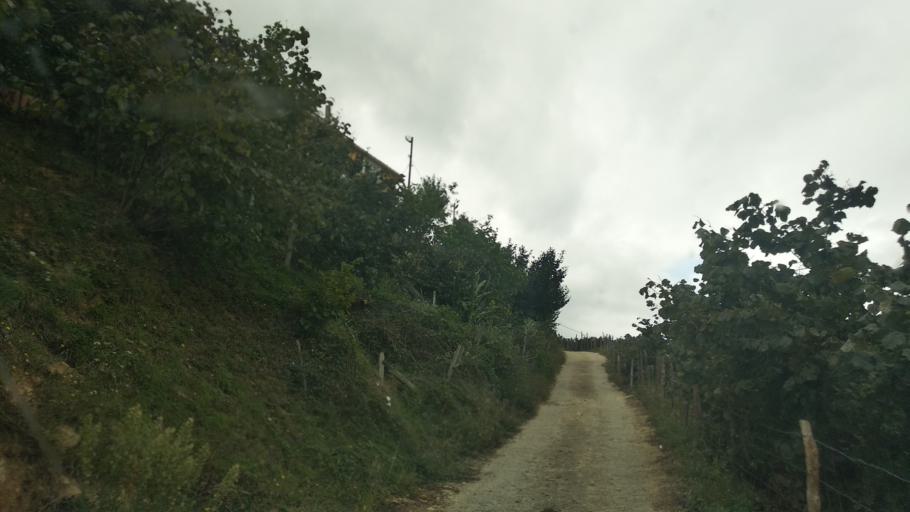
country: TR
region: Giresun
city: Dogankent
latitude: 40.7430
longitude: 38.9961
